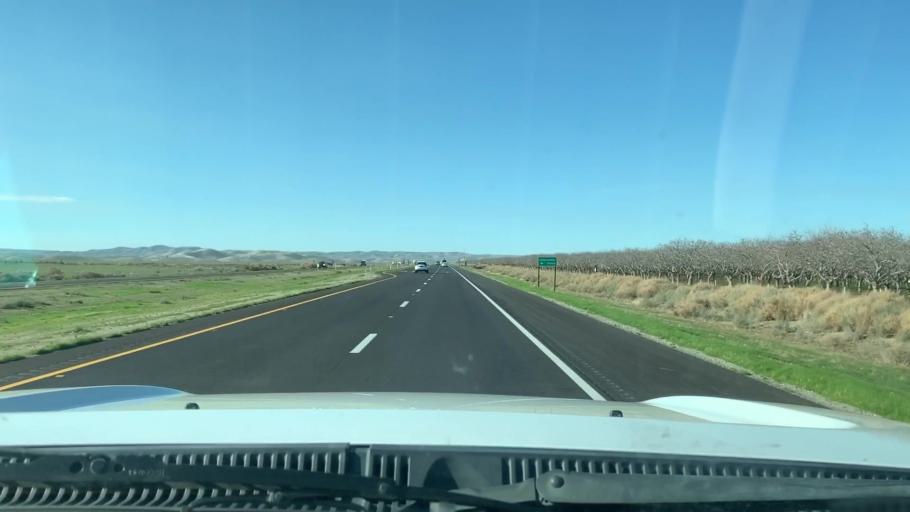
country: US
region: California
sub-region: Kern County
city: Lost Hills
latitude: 35.6147
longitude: -119.9198
